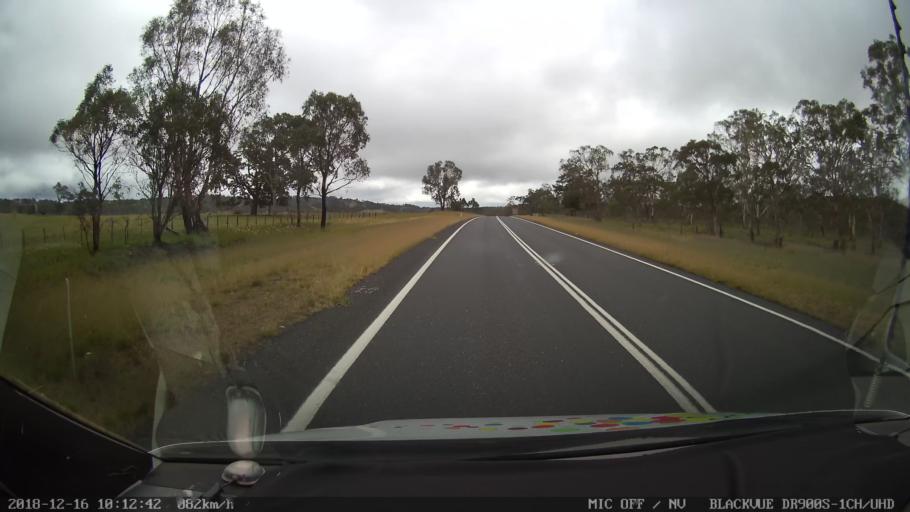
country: AU
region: New South Wales
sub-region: Glen Innes Severn
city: Glen Innes
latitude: -29.3039
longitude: 151.9436
